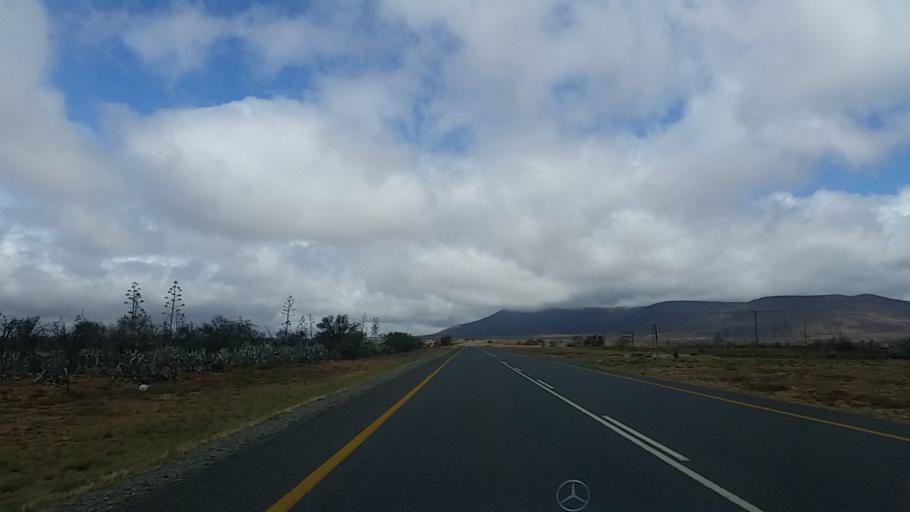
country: ZA
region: Eastern Cape
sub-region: Cacadu District Municipality
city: Graaff-Reinet
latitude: -32.0117
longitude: 24.6512
